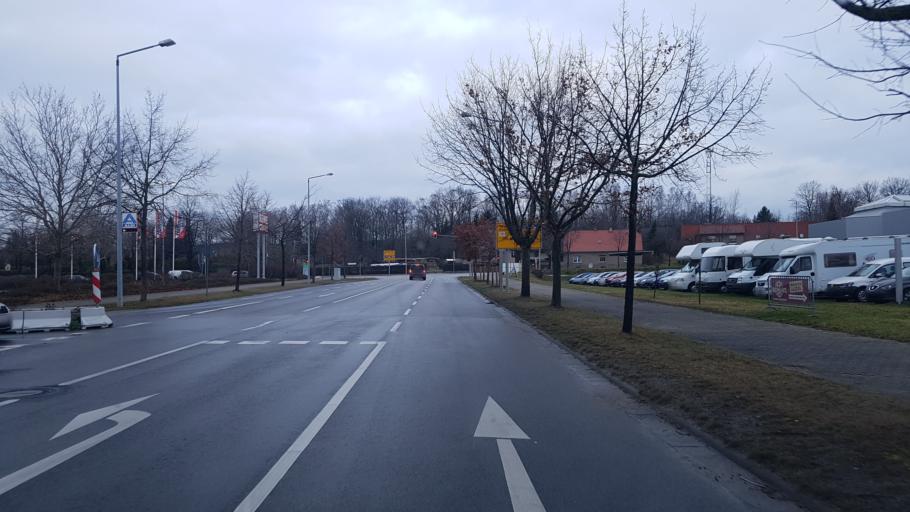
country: DE
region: Brandenburg
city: Elsterwerda
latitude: 51.4664
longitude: 13.5369
